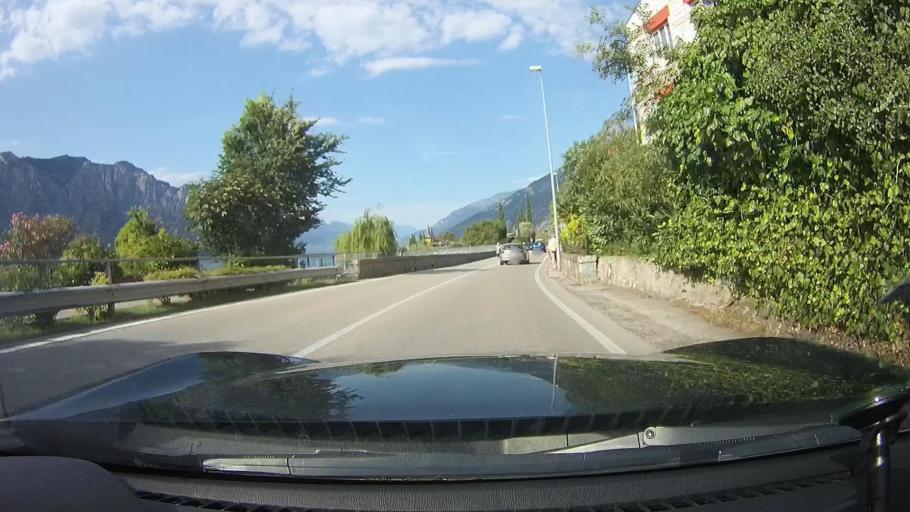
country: IT
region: Veneto
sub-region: Provincia di Verona
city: Malcesine
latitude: 45.7850
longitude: 10.8194
